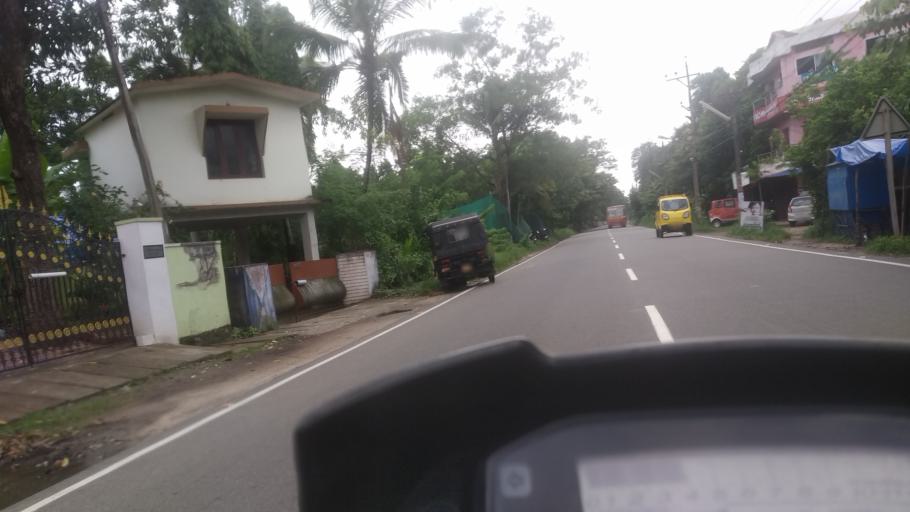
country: IN
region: Kerala
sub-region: Ernakulam
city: Elur
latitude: 10.1375
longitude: 76.2685
